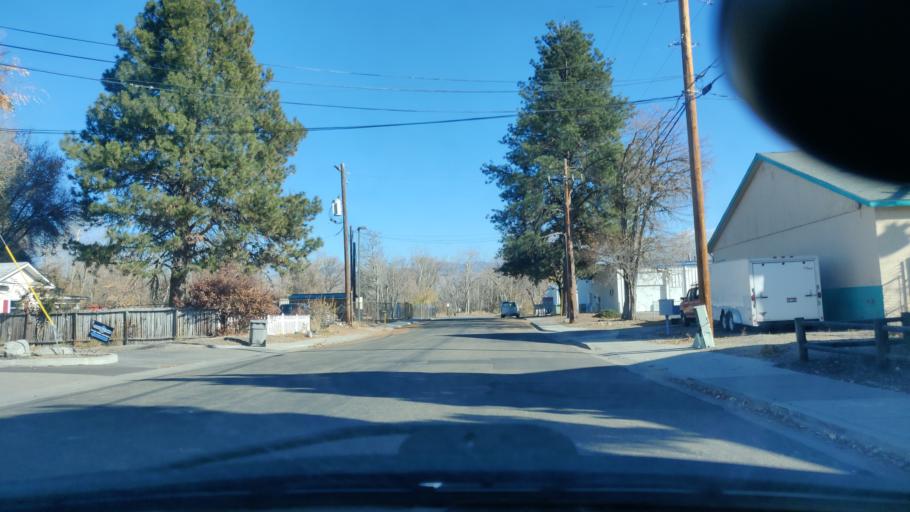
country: US
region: Idaho
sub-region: Ada County
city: Garden City
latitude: 43.6388
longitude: -116.2480
